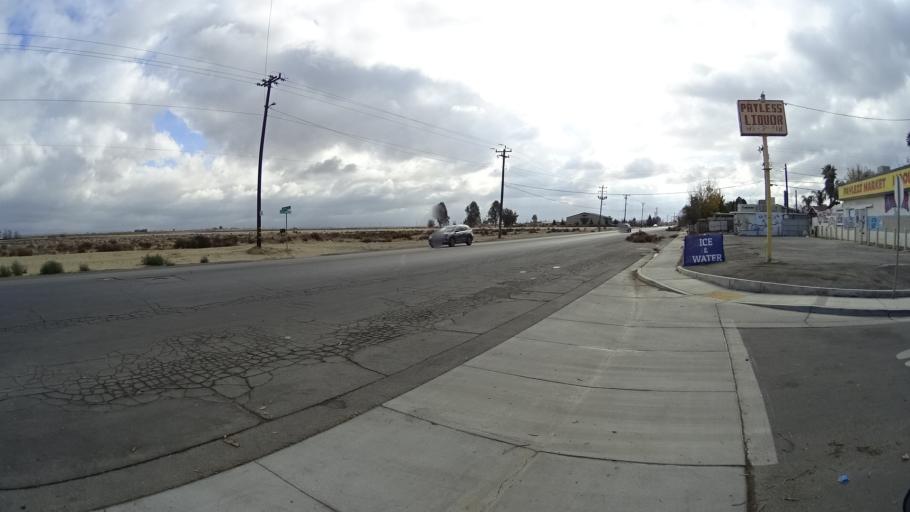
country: US
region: California
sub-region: Kern County
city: Bakersfield
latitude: 35.3314
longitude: -118.9856
